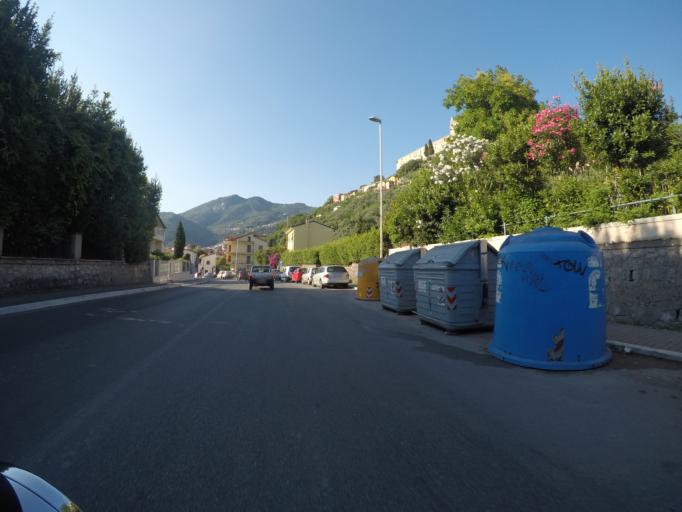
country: IT
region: Tuscany
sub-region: Provincia di Massa-Carrara
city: Massa
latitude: 44.0306
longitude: 10.1444
